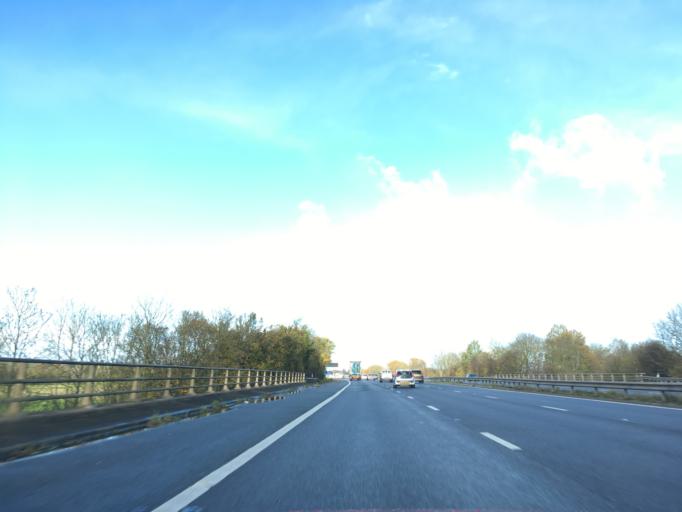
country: GB
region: England
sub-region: Worcestershire
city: Bredon
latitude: 52.0238
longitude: -2.1217
